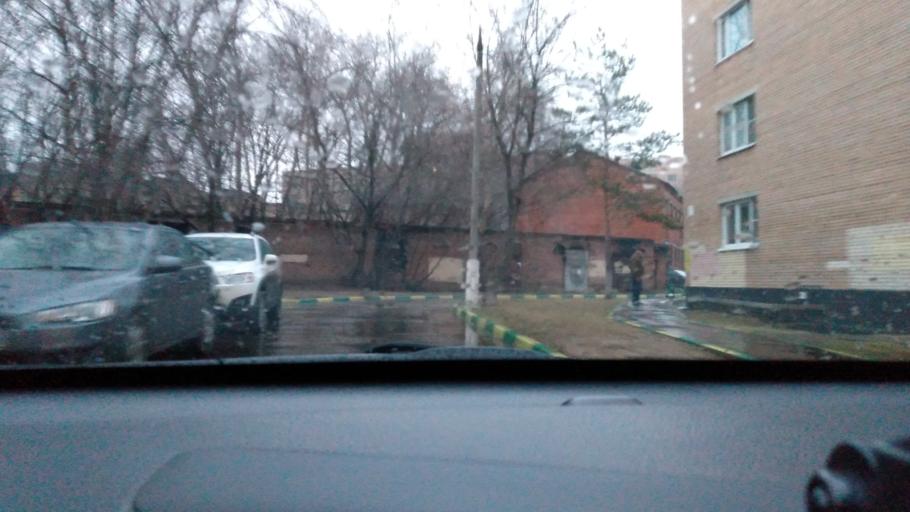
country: RU
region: Moskovskaya
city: Lyubertsy
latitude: 55.6761
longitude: 37.8716
